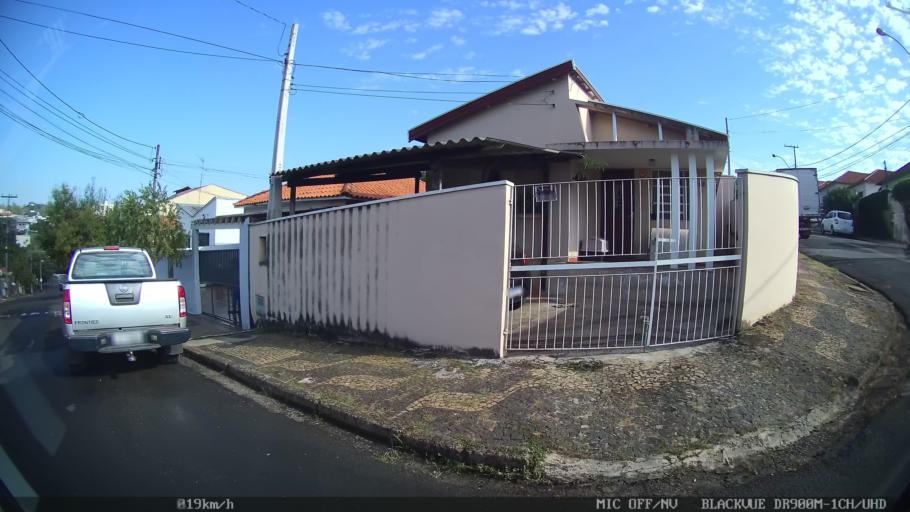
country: BR
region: Sao Paulo
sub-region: Americana
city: Americana
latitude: -22.7342
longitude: -47.3399
